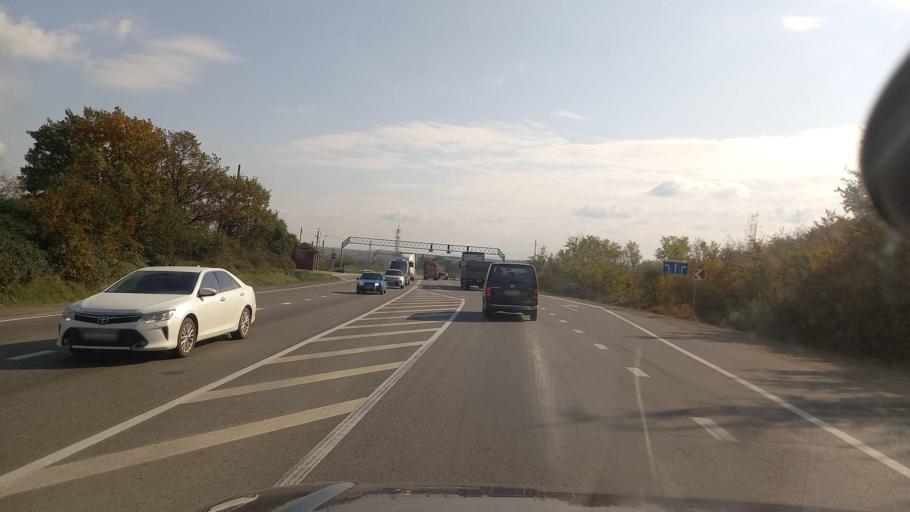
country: RU
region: Krasnodarskiy
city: Abinsk
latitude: 44.8485
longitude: 38.1400
